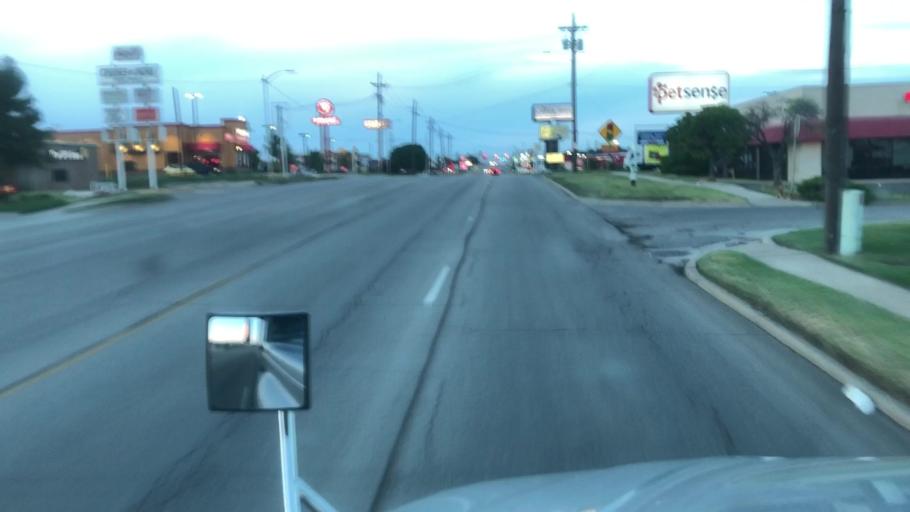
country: US
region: Oklahoma
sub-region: Kay County
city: Ponca City
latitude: 36.7290
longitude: -97.0672
